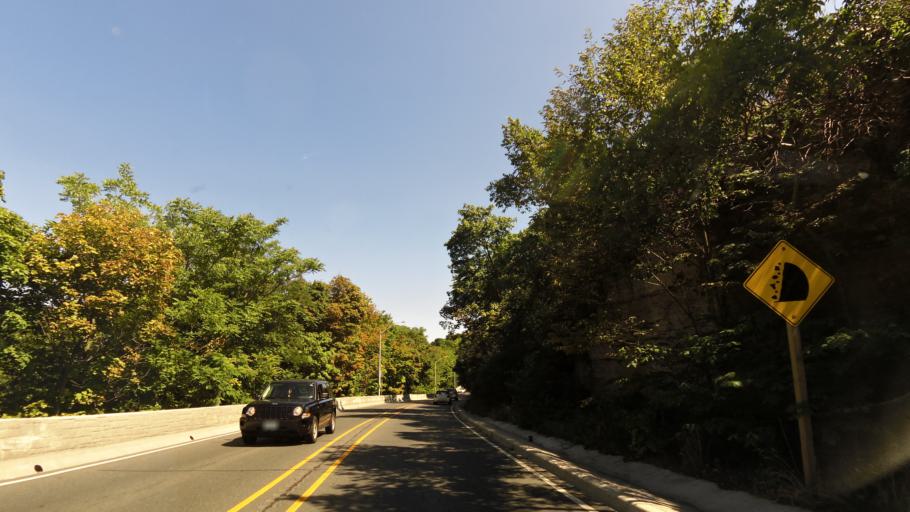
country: CA
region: Ontario
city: Hamilton
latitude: 43.2448
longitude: -79.8948
